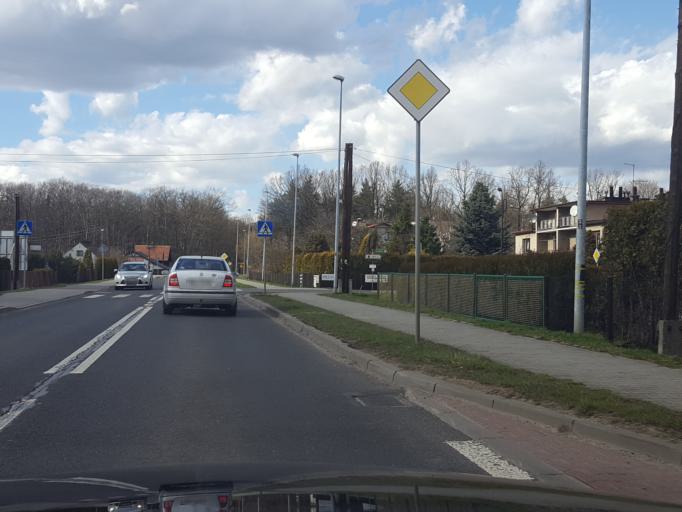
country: PL
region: Silesian Voivodeship
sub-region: Powiat pszczynski
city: Kobior
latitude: 50.0664
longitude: 18.9168
